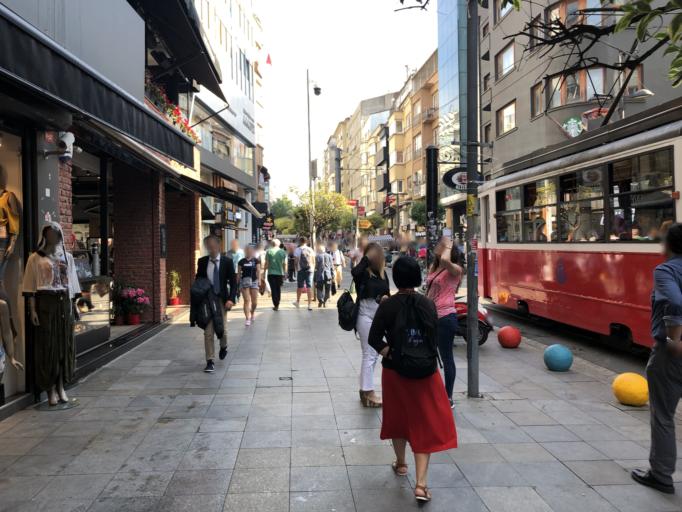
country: TR
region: Istanbul
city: UEskuedar
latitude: 40.9895
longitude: 29.0289
